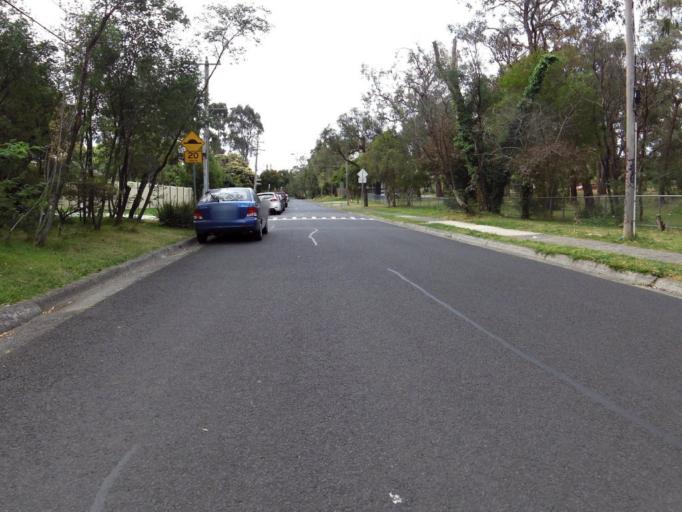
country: AU
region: Victoria
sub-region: Knox
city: Wantirna
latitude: -37.8370
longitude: 145.2303
